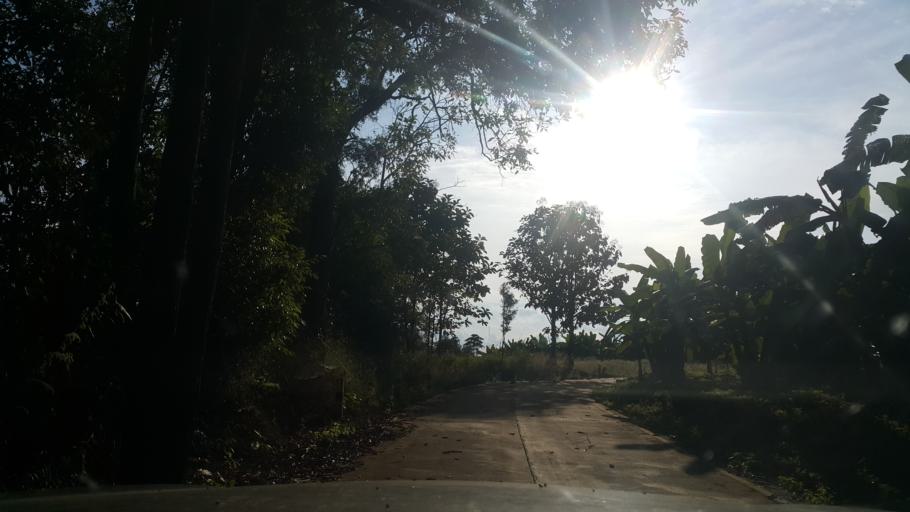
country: TH
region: Chiang Mai
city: Samoeng
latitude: 19.0005
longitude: 98.6839
